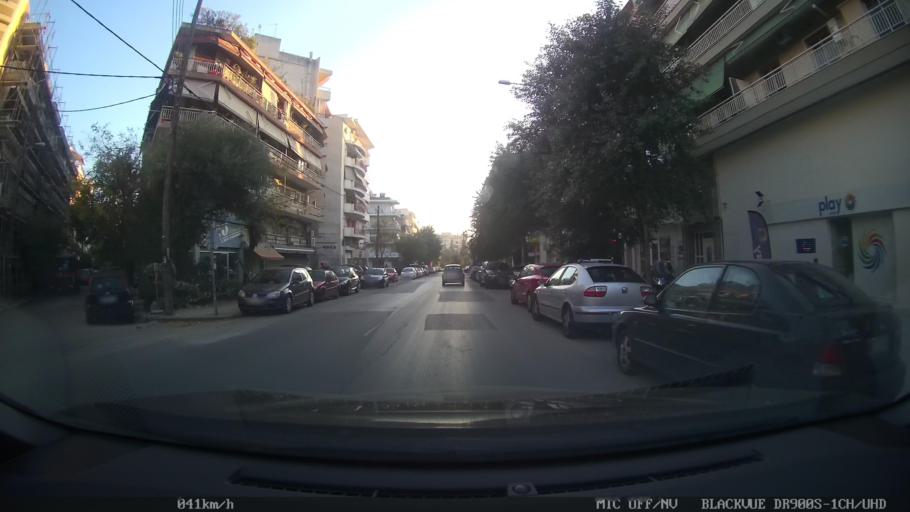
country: GR
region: Central Macedonia
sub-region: Nomos Thessalonikis
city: Triandria
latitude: 40.6065
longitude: 22.9753
